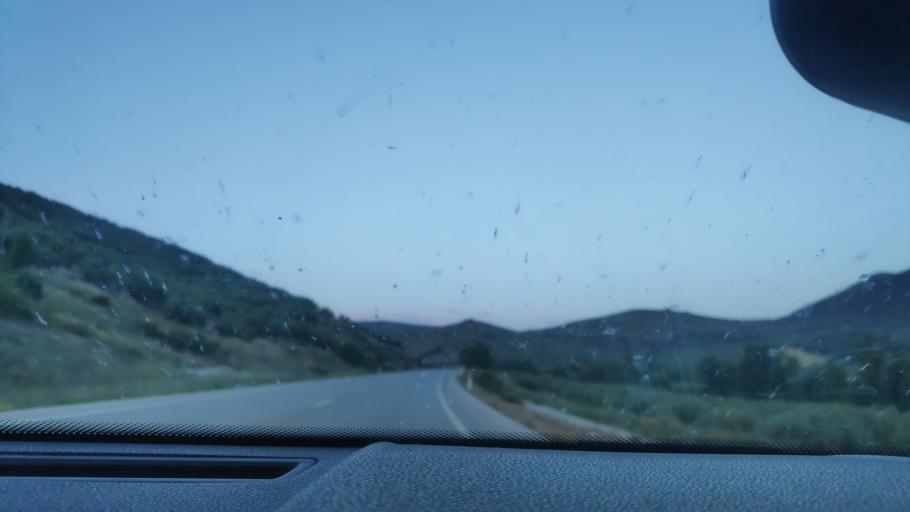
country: ES
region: Andalusia
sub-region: Provincia de Granada
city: Benalua de las Villas
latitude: 37.4390
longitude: -3.6597
